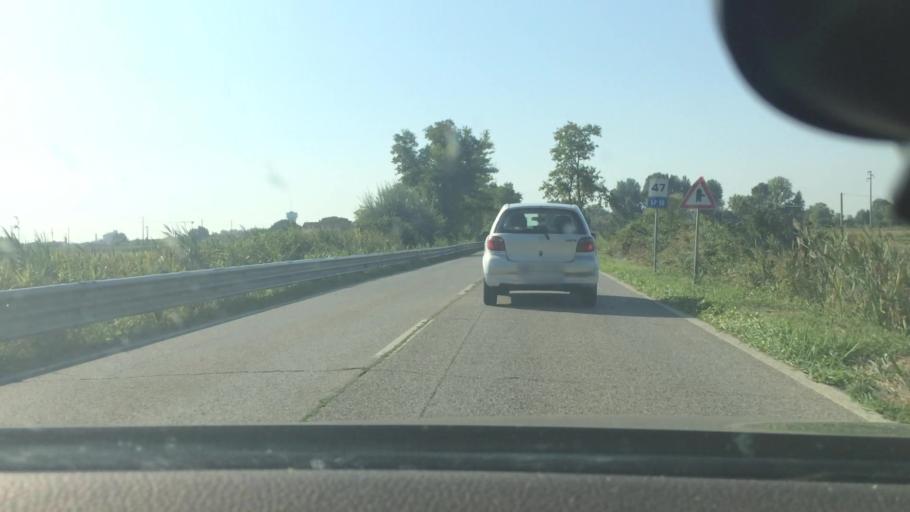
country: IT
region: Emilia-Romagna
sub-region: Provincia di Ferrara
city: Comacchio
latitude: 44.7076
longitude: 12.1628
